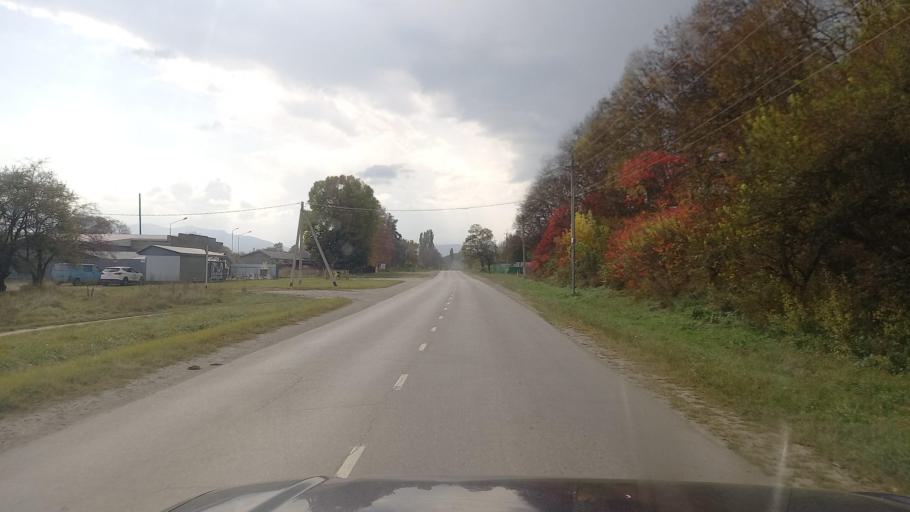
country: RU
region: Krasnodarskiy
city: Psebay
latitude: 44.1359
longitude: 40.8162
